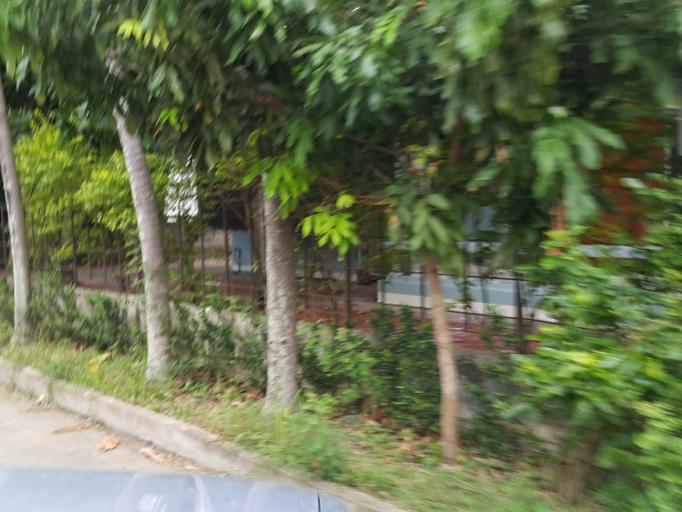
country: TH
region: Chiang Mai
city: Saraphi
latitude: 18.6939
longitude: 99.0310
